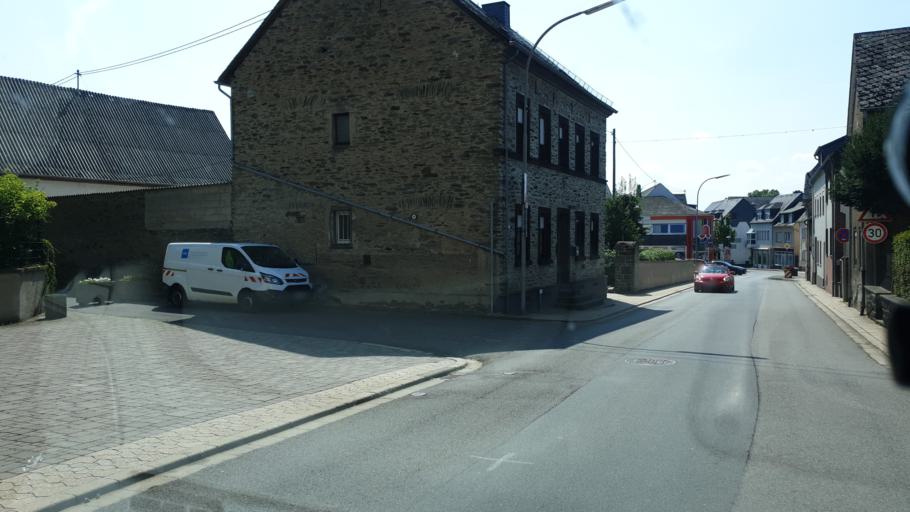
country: DE
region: Rheinland-Pfalz
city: Polch
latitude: 50.3014
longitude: 7.3107
